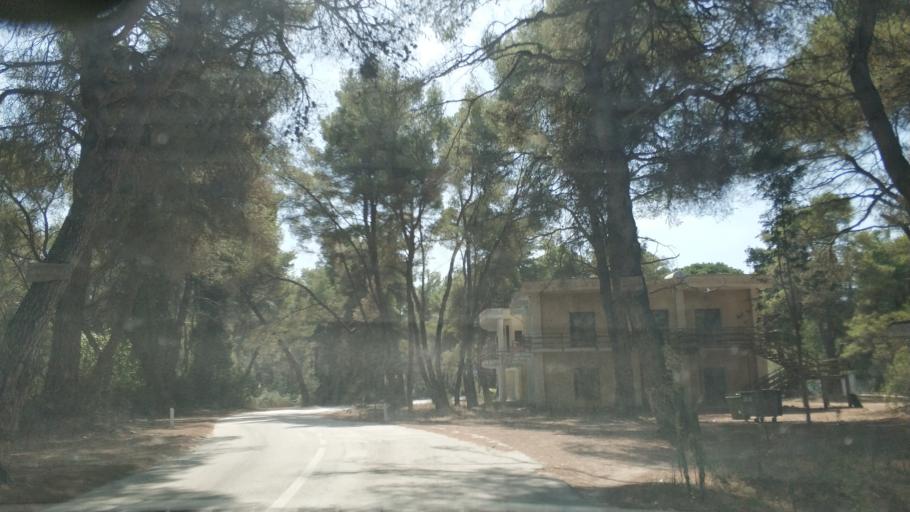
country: AL
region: Fier
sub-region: Rrethi i Lushnjes
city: Divjake
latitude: 40.9830
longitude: 19.4825
